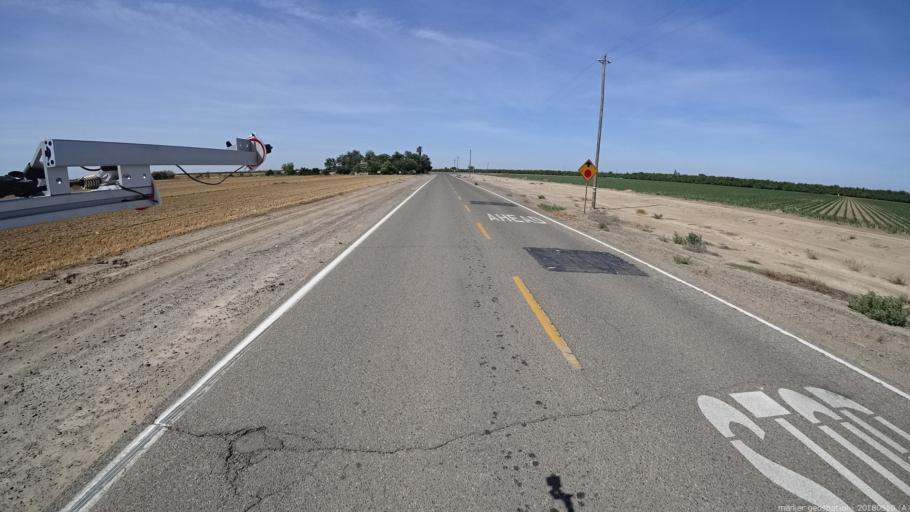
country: US
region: California
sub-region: Madera County
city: Chowchilla
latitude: 37.0200
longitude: -120.3516
